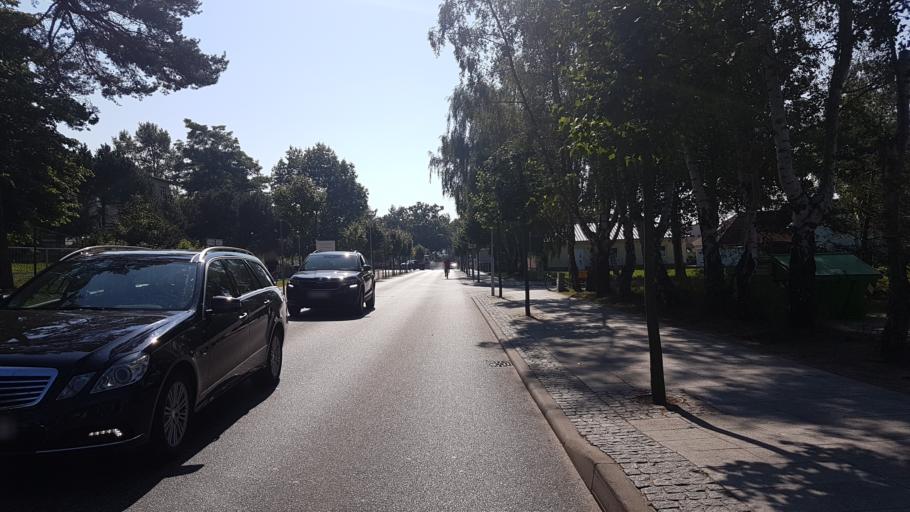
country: DE
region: Mecklenburg-Vorpommern
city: Ostseebad Sellin
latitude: 54.3731
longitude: 13.6998
